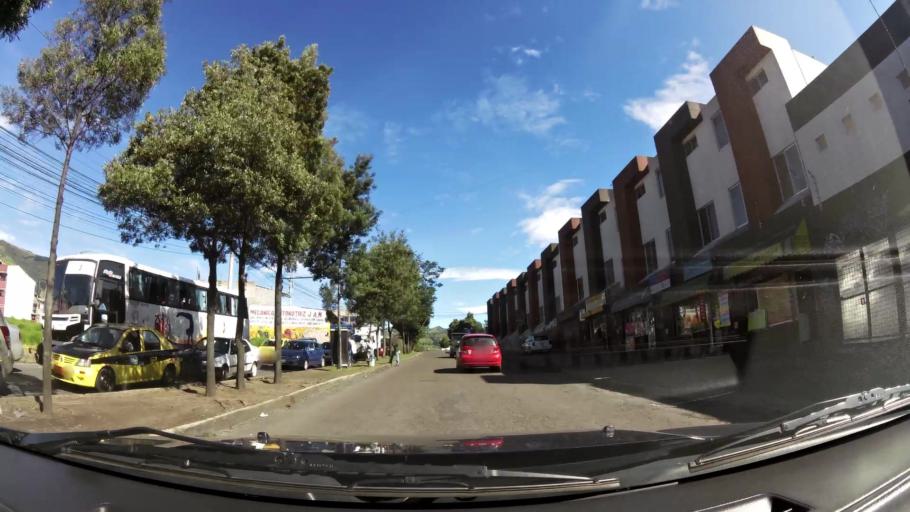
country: EC
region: Pichincha
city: Quito
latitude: -0.2916
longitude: -78.5588
